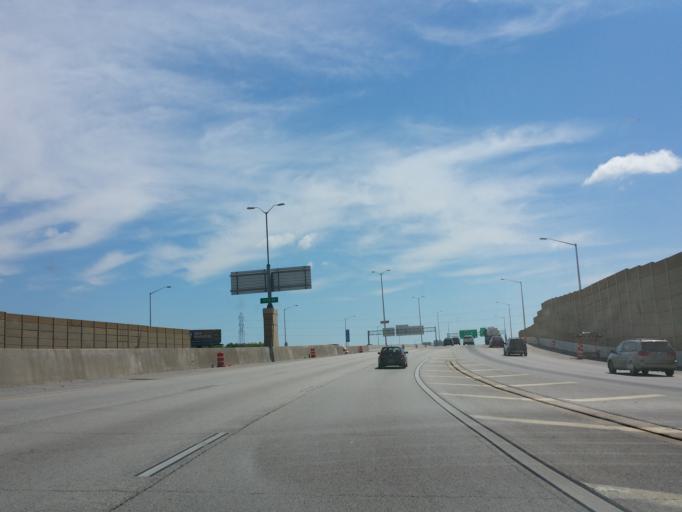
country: US
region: Wisconsin
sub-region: Milwaukee County
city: Saint Francis
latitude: 42.9656
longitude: -87.9310
